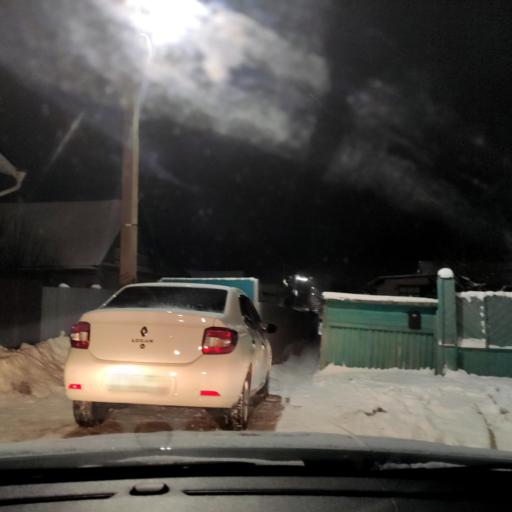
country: RU
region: Tatarstan
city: Staroye Arakchino
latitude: 55.8814
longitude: 49.0437
